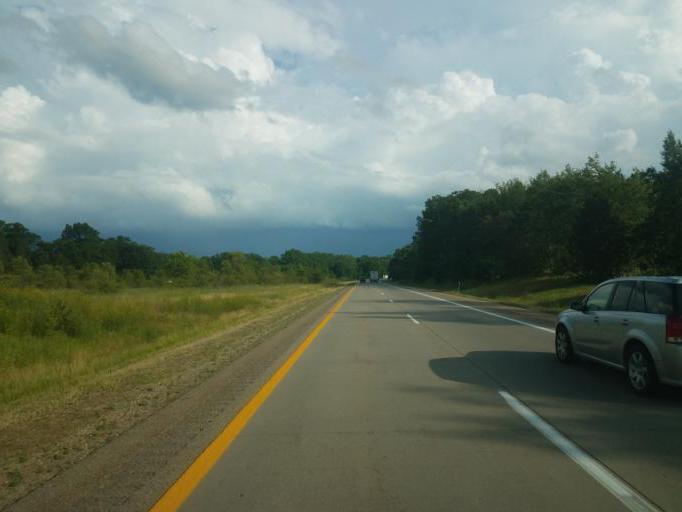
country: US
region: Michigan
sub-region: Calhoun County
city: Marshall
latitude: 42.1546
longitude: -84.9925
